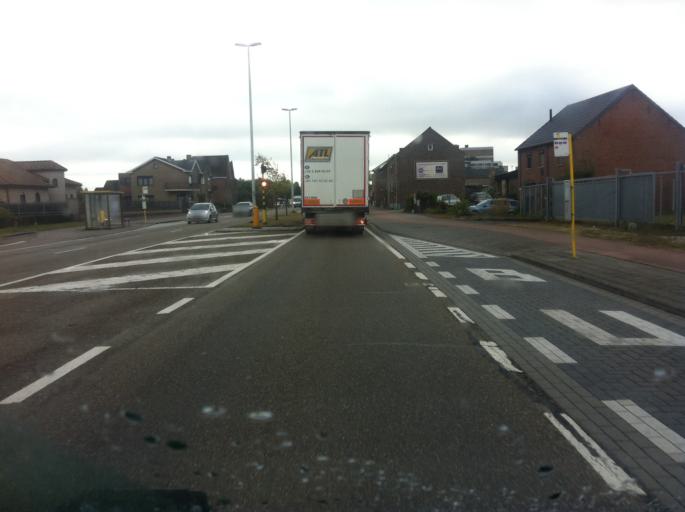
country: BE
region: Flanders
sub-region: Provincie Limburg
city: Maasmechelen
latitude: 50.9291
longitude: 5.6882
